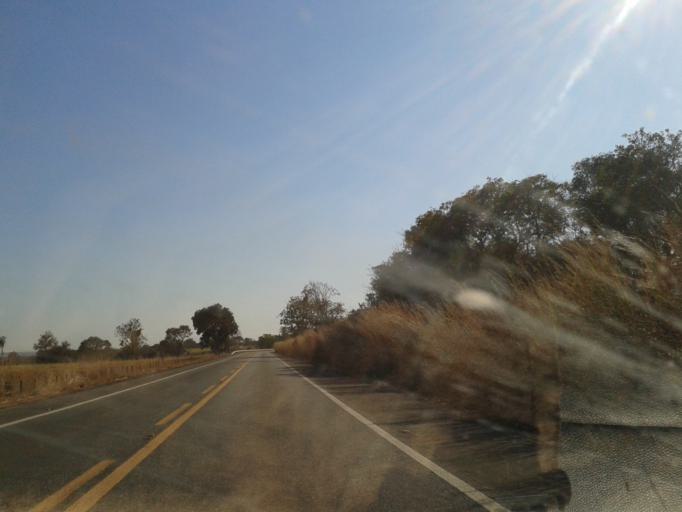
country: BR
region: Goias
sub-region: Mozarlandia
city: Mozarlandia
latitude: -14.8747
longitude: -50.5522
